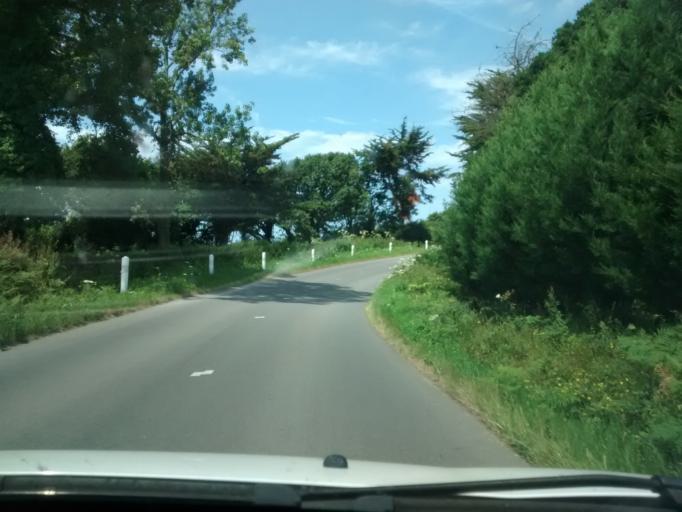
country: FR
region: Brittany
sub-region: Departement des Cotes-d'Armor
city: Trevou-Treguignec
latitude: 48.8074
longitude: -3.3281
